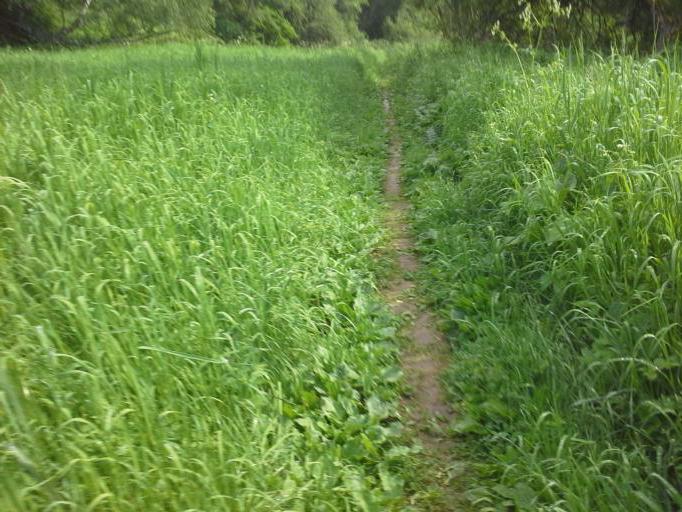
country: RU
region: Moskovskaya
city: Moskovskiy
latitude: 55.5829
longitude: 37.3396
